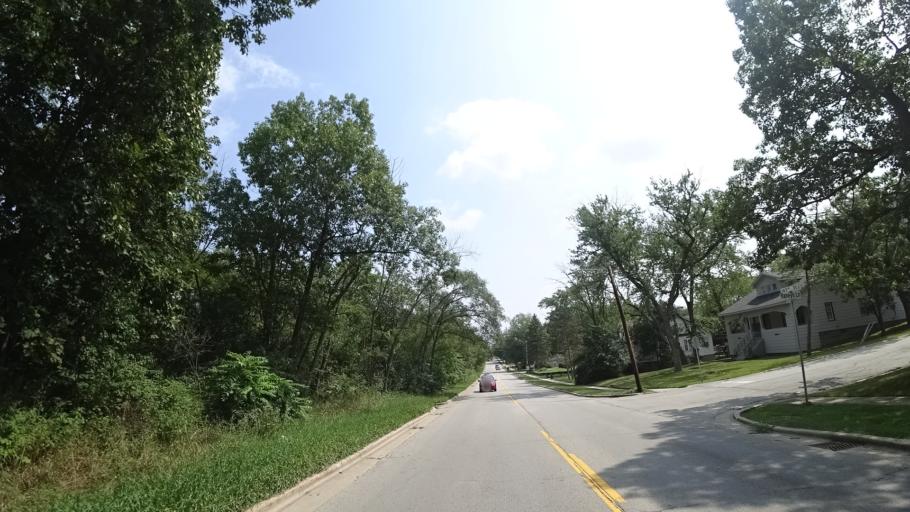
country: US
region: Illinois
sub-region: Cook County
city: Orland Park
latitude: 41.6301
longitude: -87.8694
